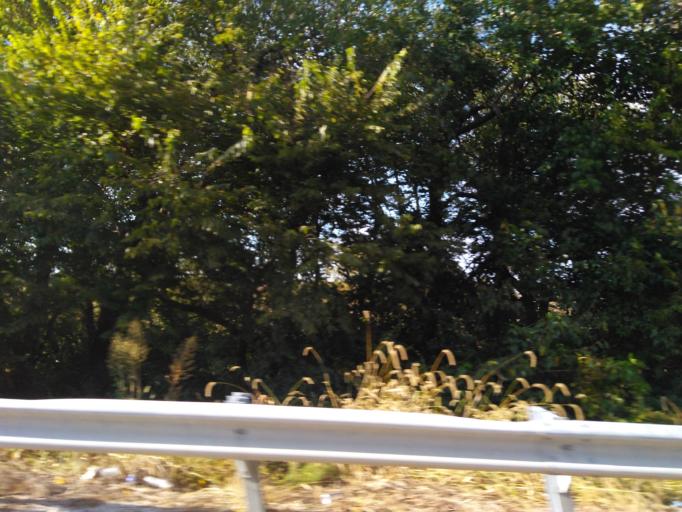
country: US
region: Illinois
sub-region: Bond County
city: Greenville
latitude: 38.8584
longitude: -89.4415
